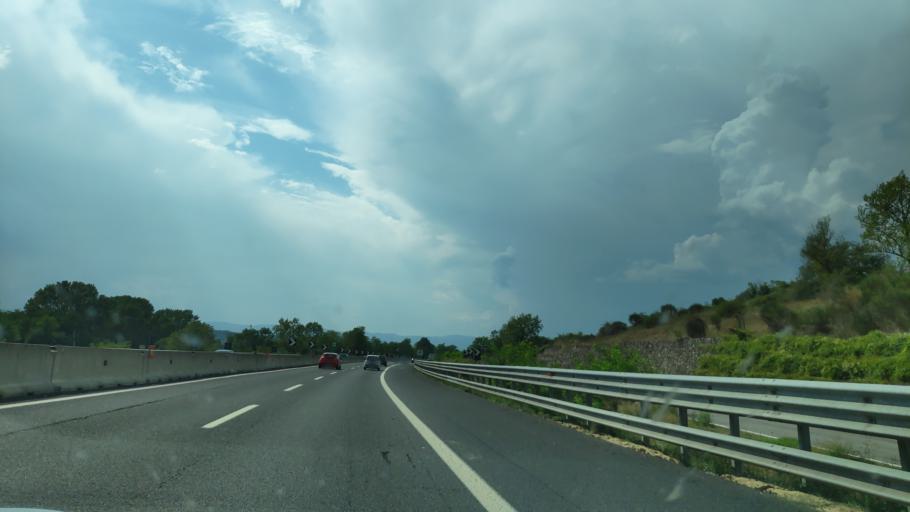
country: IT
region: Tuscany
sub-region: Province of Arezzo
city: Bucine
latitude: 43.5148
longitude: 11.6188
